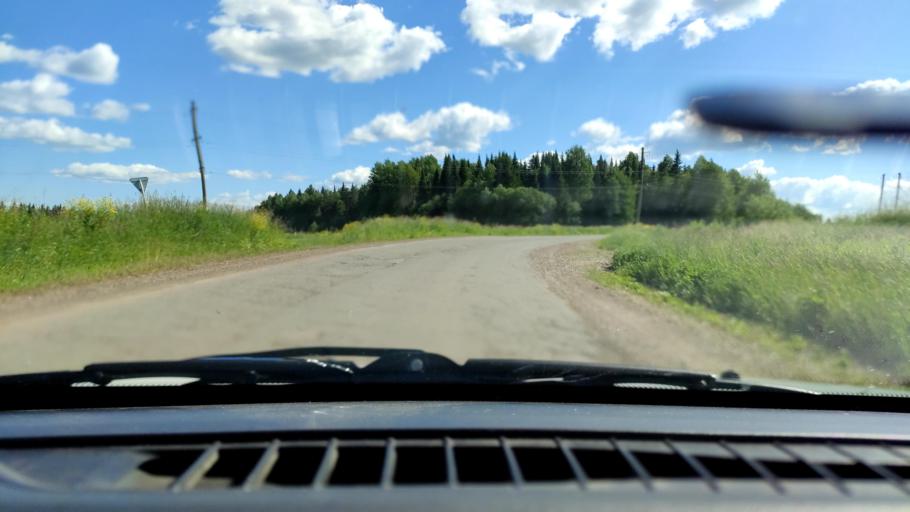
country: RU
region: Perm
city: Uinskoye
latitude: 57.1351
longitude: 56.5695
